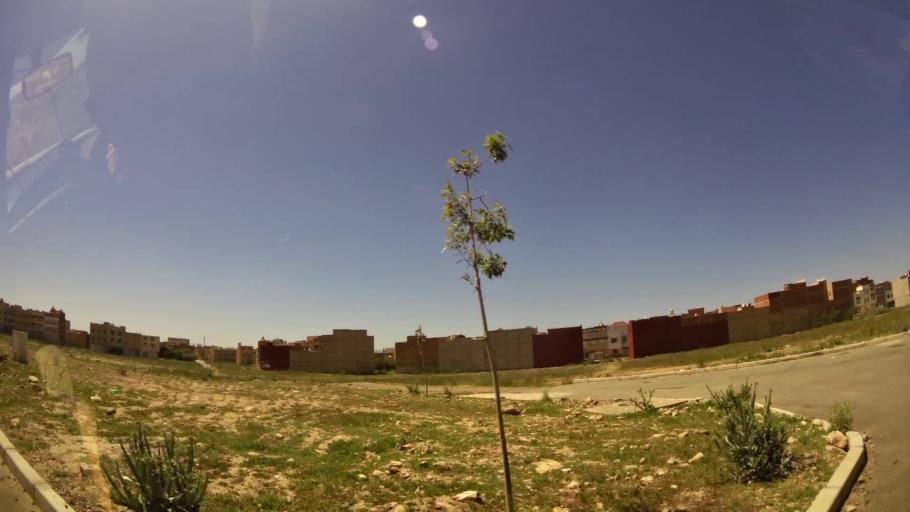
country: MA
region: Oriental
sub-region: Oujda-Angad
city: Oujda
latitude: 34.6690
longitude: -1.8674
